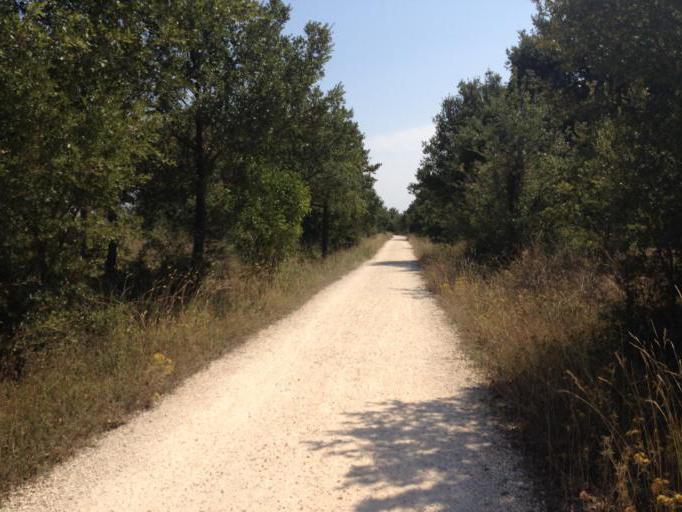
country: IT
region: Apulia
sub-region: Provincia di Brindisi
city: Cisternino
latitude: 40.7085
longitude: 17.4117
